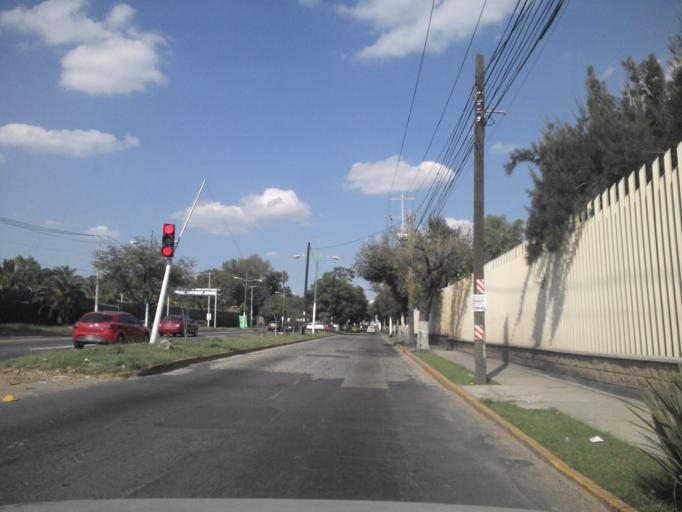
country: MX
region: Jalisco
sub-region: Tlajomulco de Zuniga
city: La Tijera
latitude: 20.6161
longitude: -103.4259
